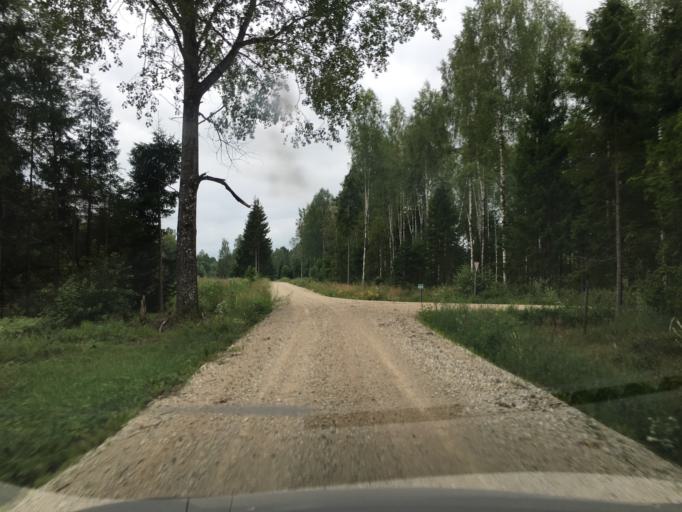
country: EE
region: Raplamaa
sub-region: Jaervakandi vald
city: Jarvakandi
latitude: 58.8051
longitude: 24.9767
